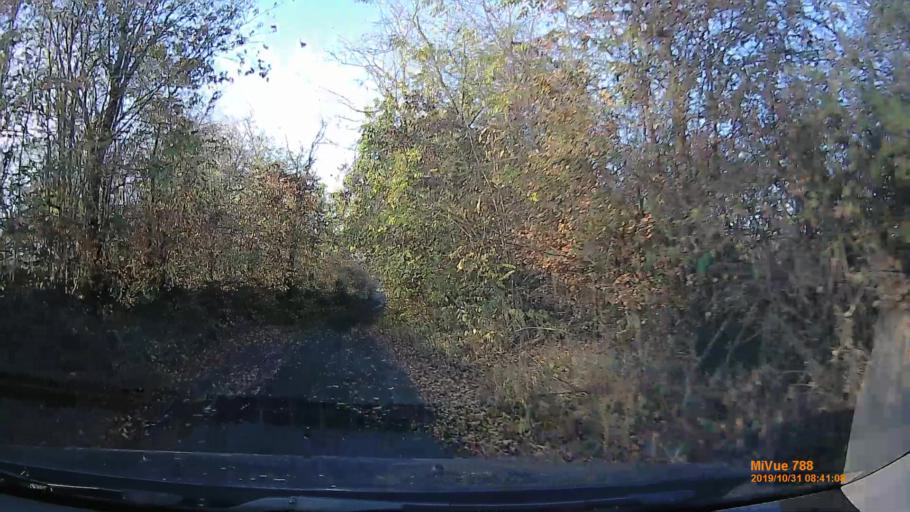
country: HU
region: Pest
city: Pand
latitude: 47.3046
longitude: 19.6428
